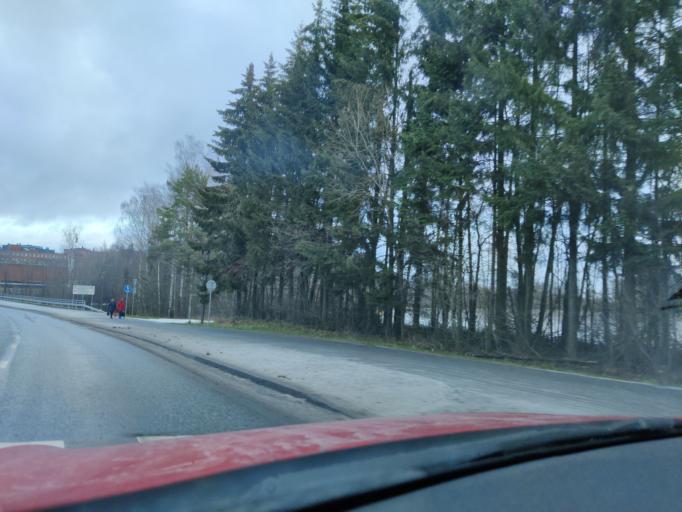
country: FI
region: Pirkanmaa
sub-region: Tampere
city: Nokia
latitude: 61.4711
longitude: 23.5049
